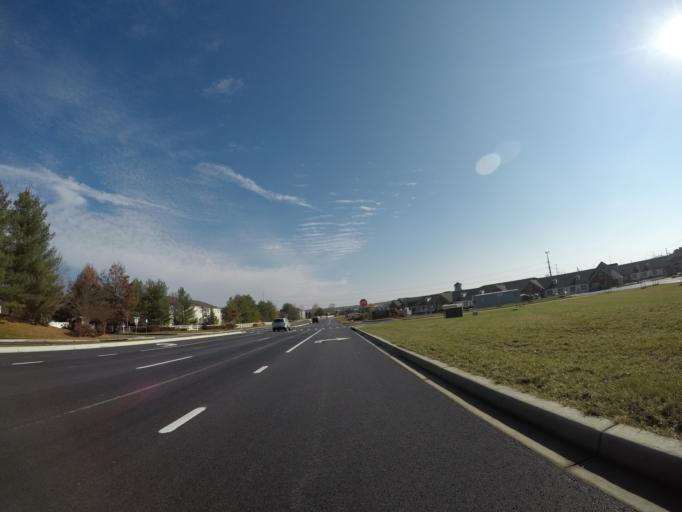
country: US
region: Maryland
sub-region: Frederick County
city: Ballenger Creek
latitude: 39.3651
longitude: -77.4384
